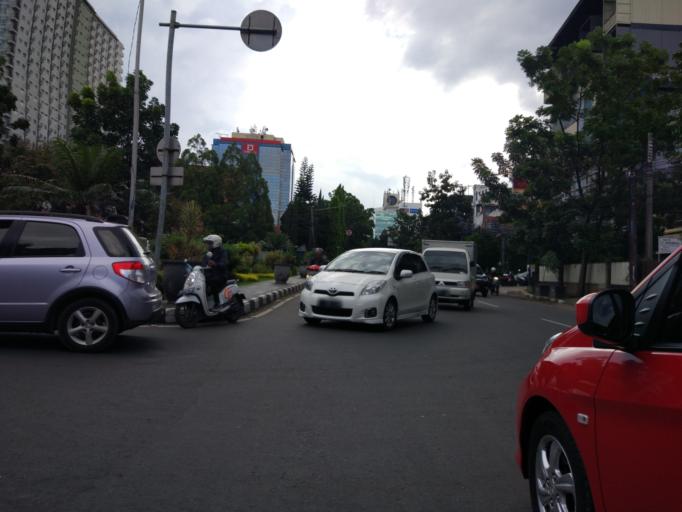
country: ID
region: West Java
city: Bandung
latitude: -6.9228
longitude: 107.6201
